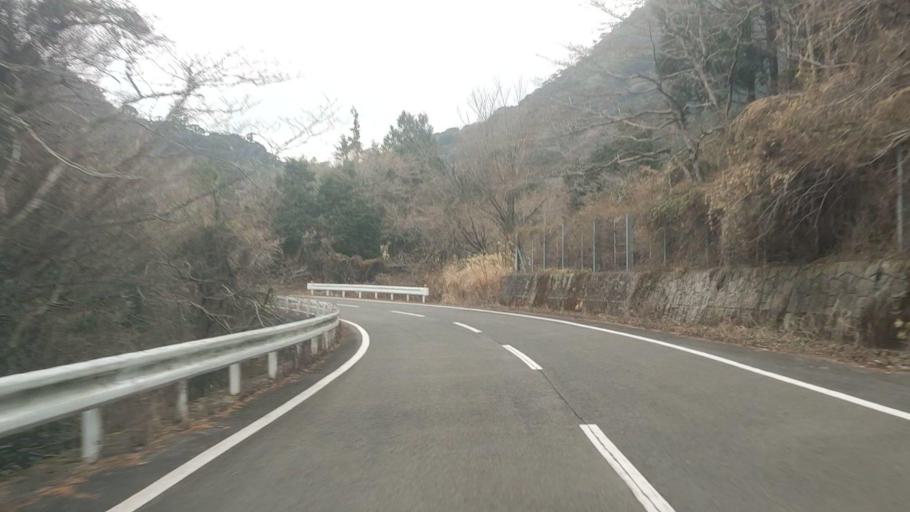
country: JP
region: Nagasaki
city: Shimabara
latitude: 32.7844
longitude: 130.2769
